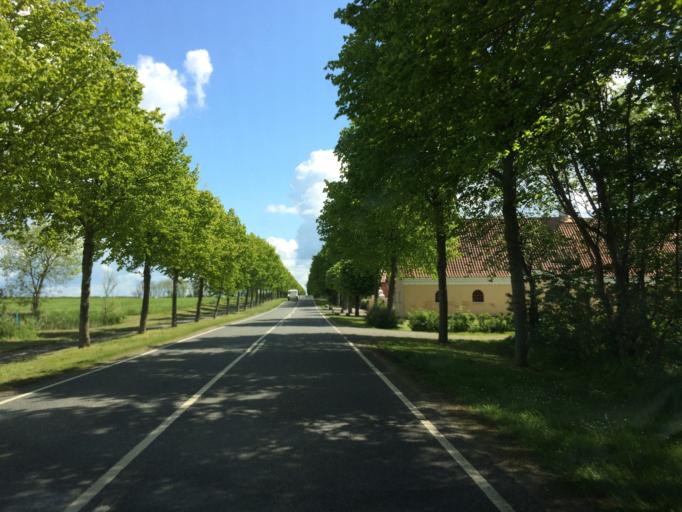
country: DK
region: Zealand
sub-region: Lejre Kommune
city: Lejre
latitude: 55.6152
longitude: 11.9958
